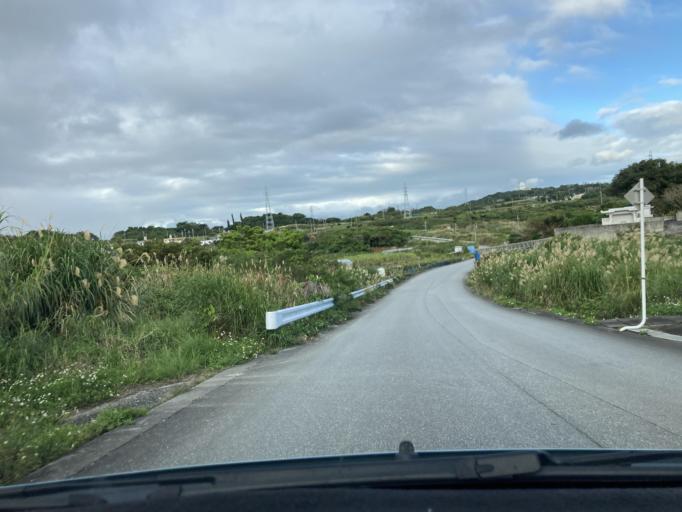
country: JP
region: Okinawa
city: Itoman
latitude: 26.1170
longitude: 127.6825
